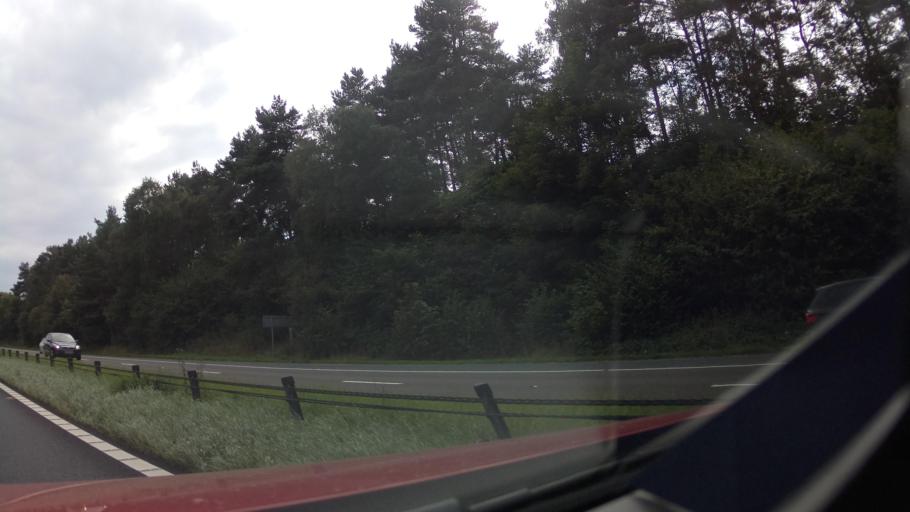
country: GB
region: England
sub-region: County Durham
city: Durham
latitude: 54.7841
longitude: -1.5332
